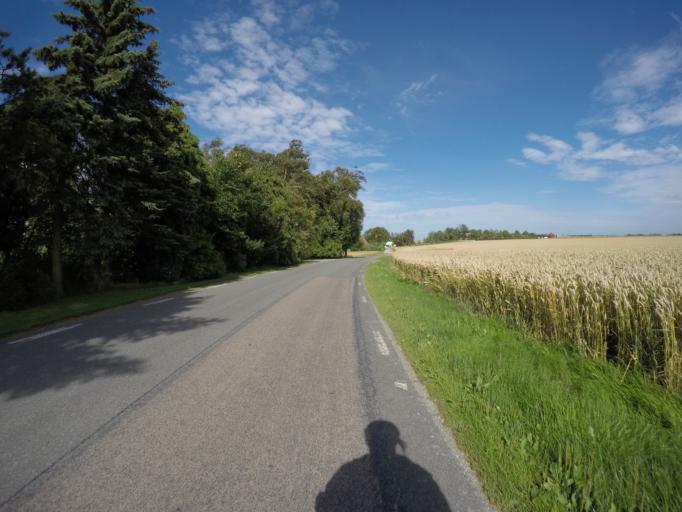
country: SE
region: Skane
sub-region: Simrishamns Kommun
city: Simrishamn
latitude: 55.4946
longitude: 14.1998
